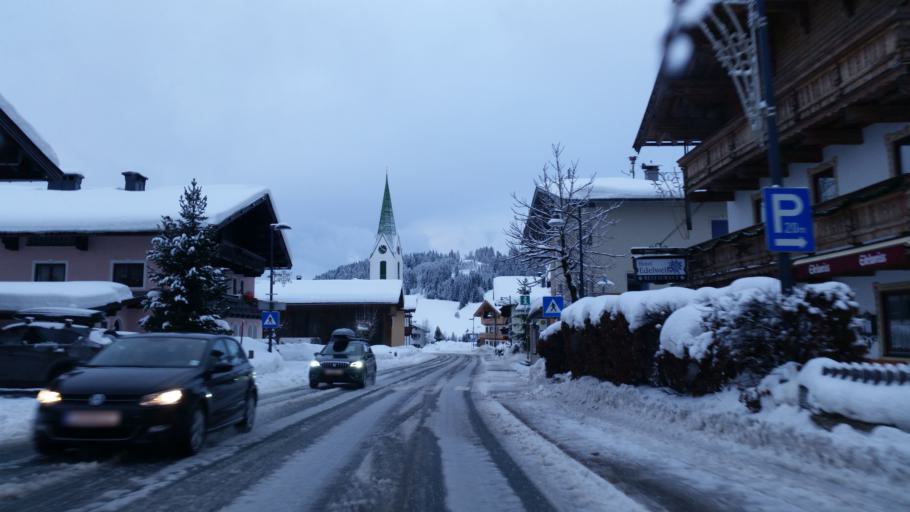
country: AT
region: Tyrol
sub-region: Politischer Bezirk Kitzbuhel
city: Hochfilzen
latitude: 47.4696
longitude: 12.6190
